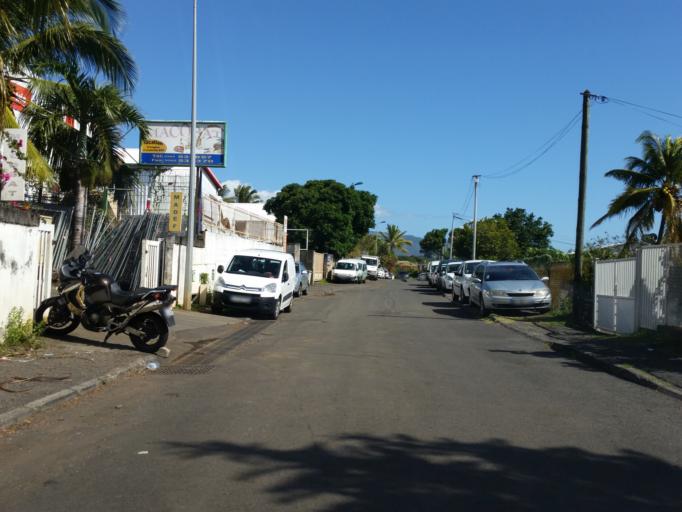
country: RE
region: Reunion
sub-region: Reunion
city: Sainte-Marie
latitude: -20.8963
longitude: 55.5322
